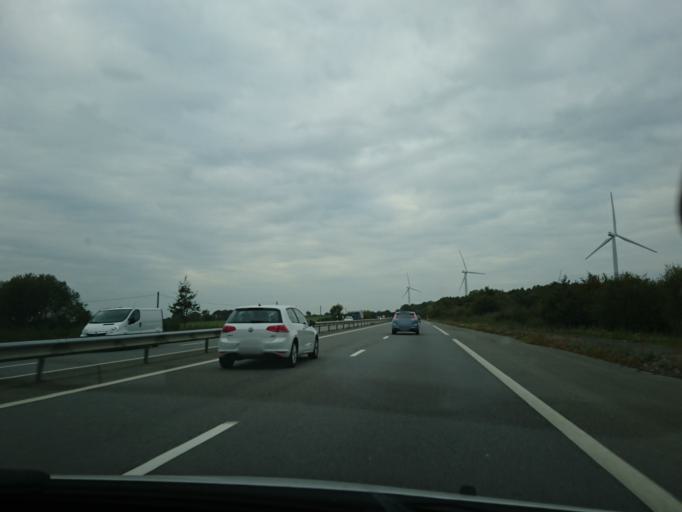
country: FR
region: Pays de la Loire
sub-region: Departement de la Loire-Atlantique
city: Prinquiau
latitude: 47.4060
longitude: -2.0122
